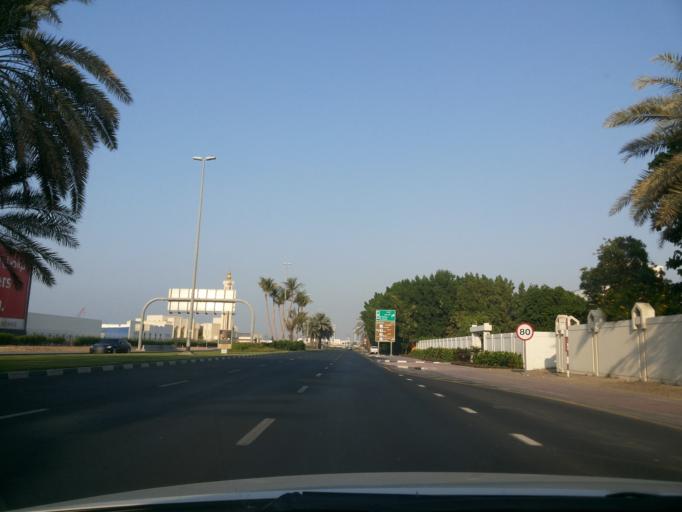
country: AE
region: Ash Shariqah
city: Sharjah
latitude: 25.2992
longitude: 55.3369
